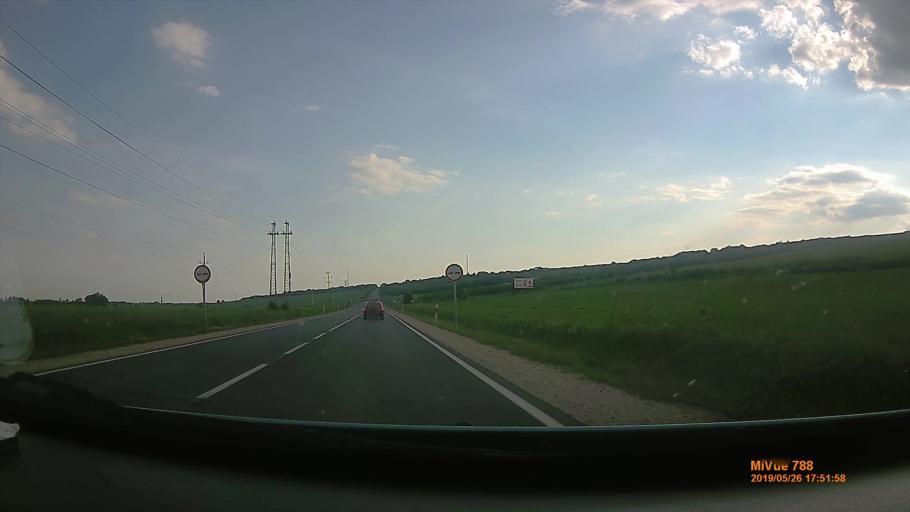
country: HU
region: Borsod-Abauj-Zemplen
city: Szikszo
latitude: 48.1694
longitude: 20.9102
